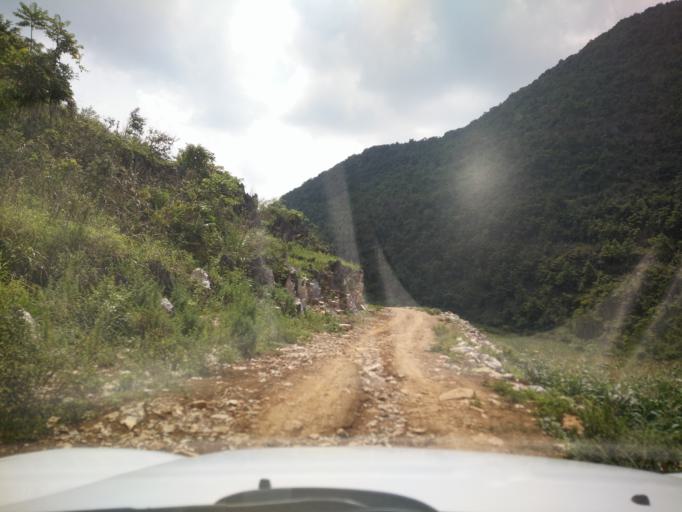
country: CN
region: Guangxi Zhuangzu Zizhiqu
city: Xinzhou
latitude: 25.1333
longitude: 105.6694
